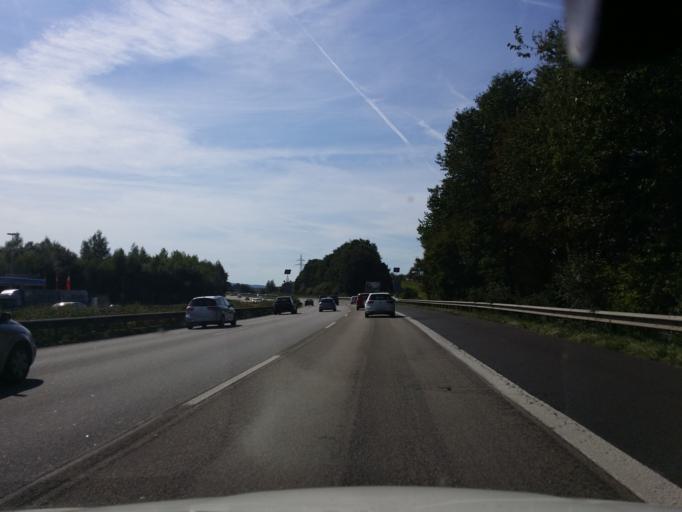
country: DE
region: Rheinland-Pfalz
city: Heiligenroth
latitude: 50.4550
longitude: 7.8677
